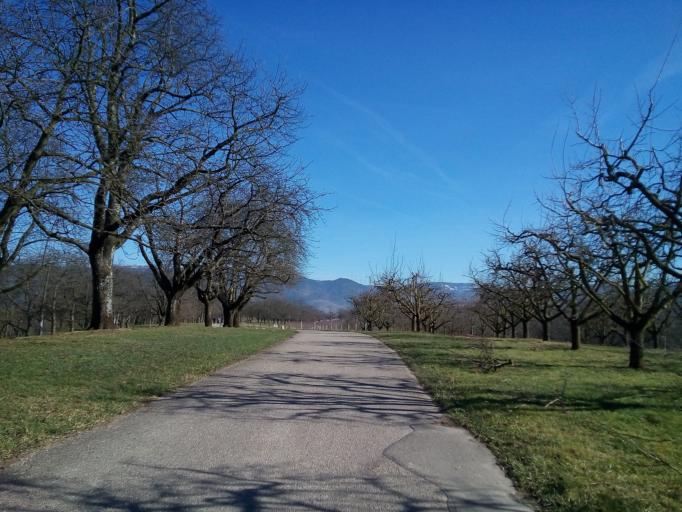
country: DE
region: Baden-Wuerttemberg
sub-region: Freiburg Region
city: Achern
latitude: 48.6068
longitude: 8.0527
